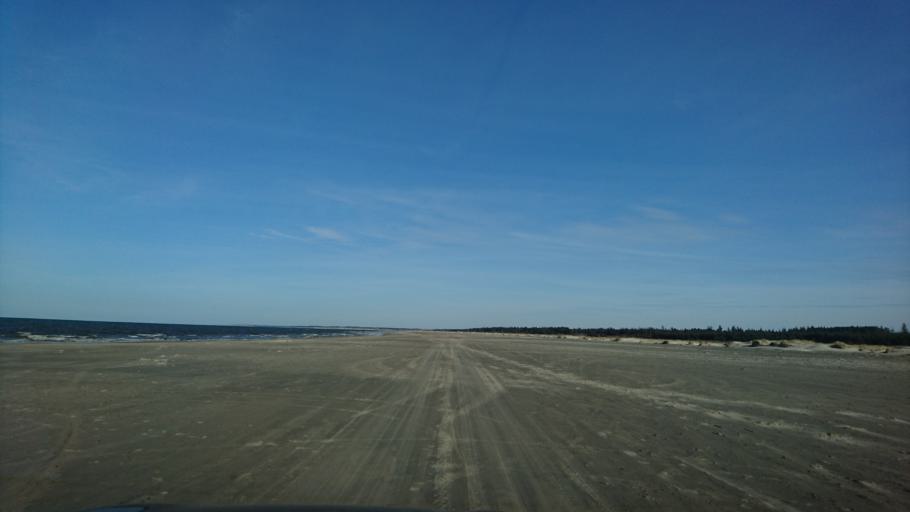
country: DK
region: North Denmark
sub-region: Hjorring Kommune
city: Hirtshals
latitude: 57.5899
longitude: 10.0781
